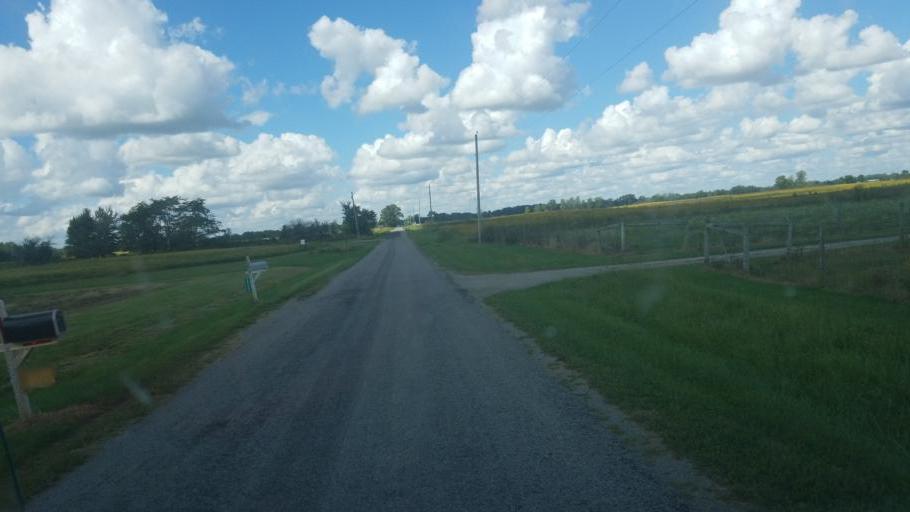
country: US
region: Ohio
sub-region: Hardin County
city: Kenton
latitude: 40.4787
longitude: -83.4983
